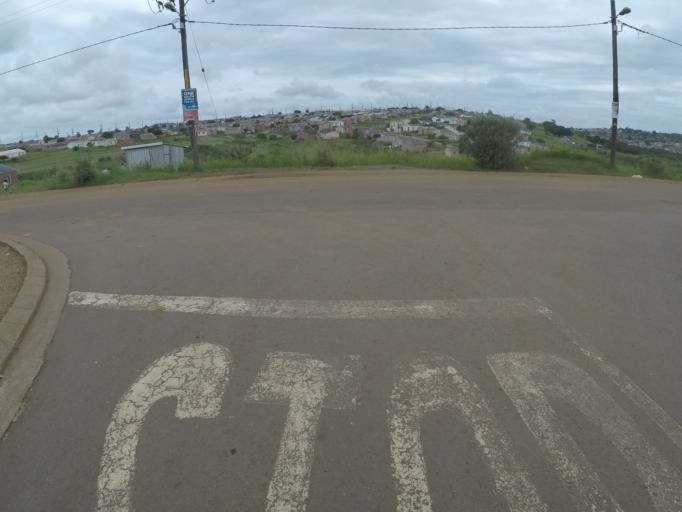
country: ZA
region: KwaZulu-Natal
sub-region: uThungulu District Municipality
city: Empangeni
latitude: -28.7649
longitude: 31.8770
